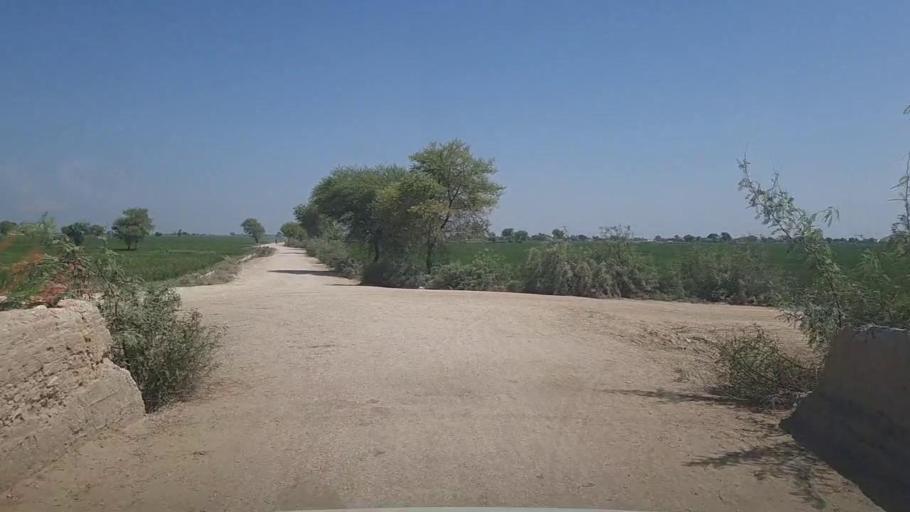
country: PK
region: Sindh
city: Kashmor
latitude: 28.2980
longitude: 69.4300
